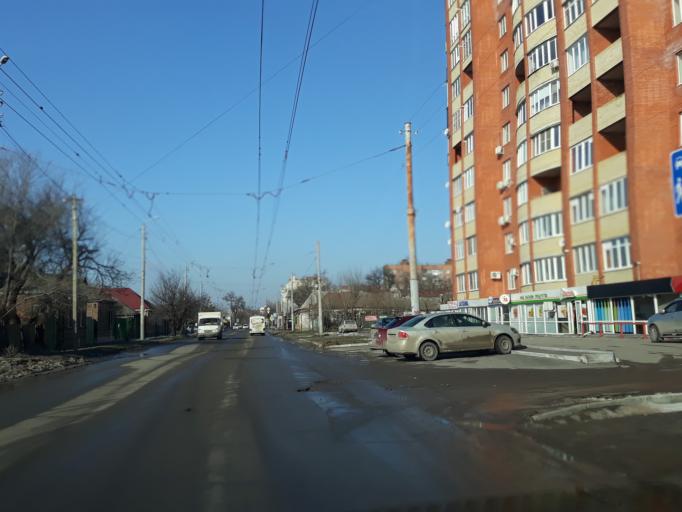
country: RU
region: Rostov
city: Taganrog
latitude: 47.2018
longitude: 38.9062
